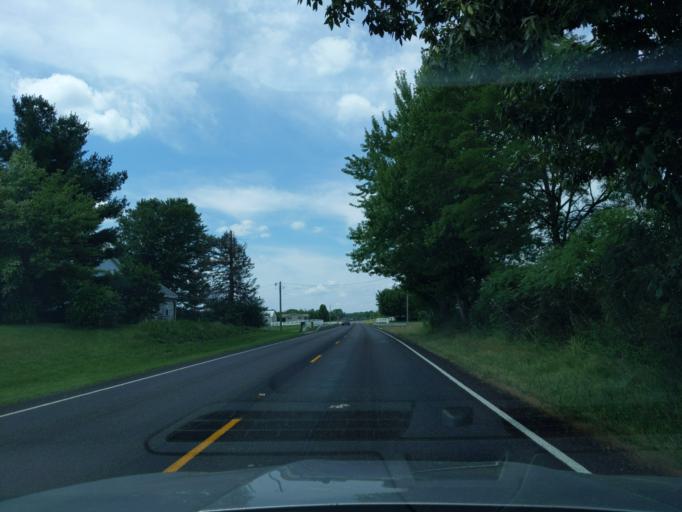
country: US
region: Indiana
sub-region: Decatur County
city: Greensburg
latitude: 39.2871
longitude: -85.4129
